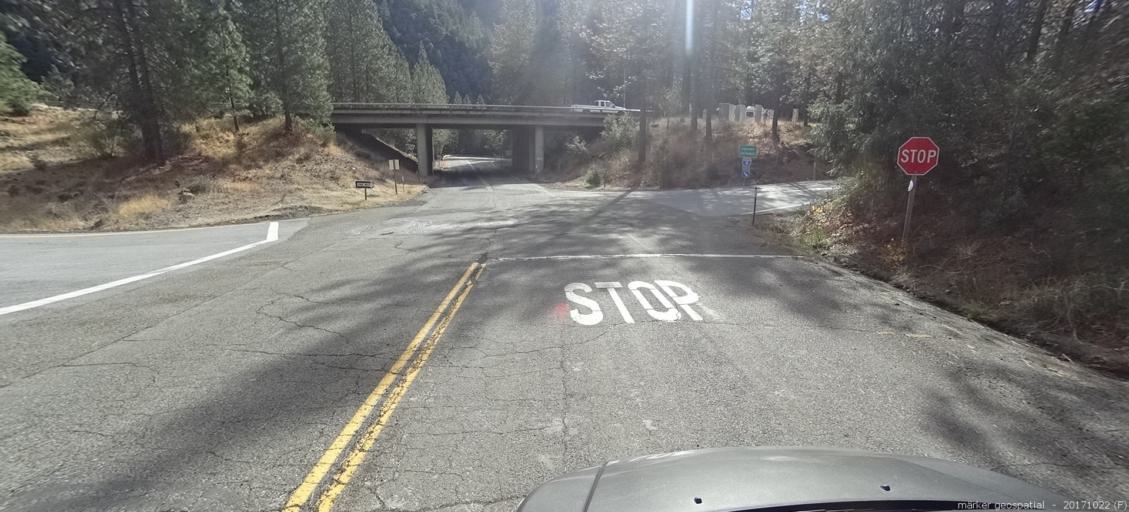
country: US
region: California
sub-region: Siskiyou County
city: Dunsmuir
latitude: 41.0722
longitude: -122.3588
